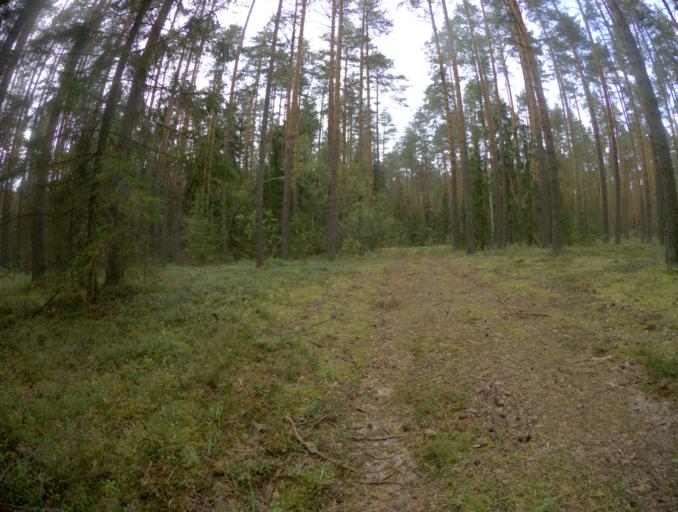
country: RU
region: Vladimir
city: Golovino
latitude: 55.8679
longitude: 40.3882
